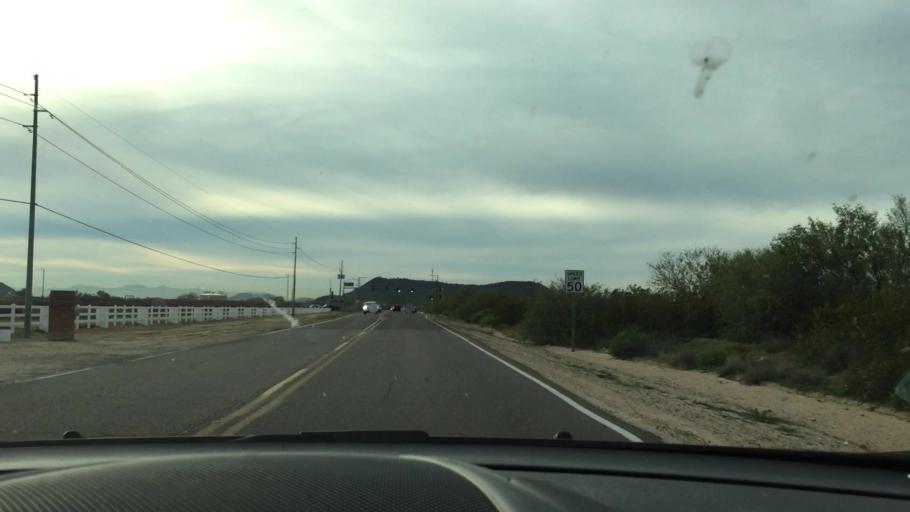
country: US
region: Arizona
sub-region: Maricopa County
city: Cave Creek
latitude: 33.6988
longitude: -112.0028
